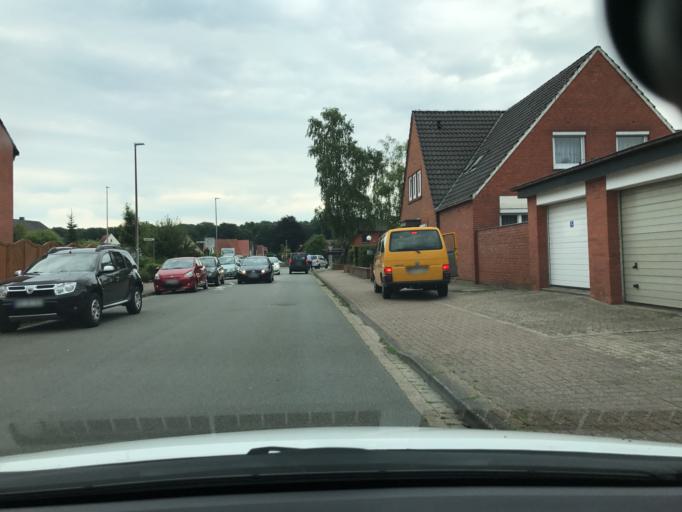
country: DE
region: Lower Saxony
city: Riede
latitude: 52.9871
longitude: 8.8692
